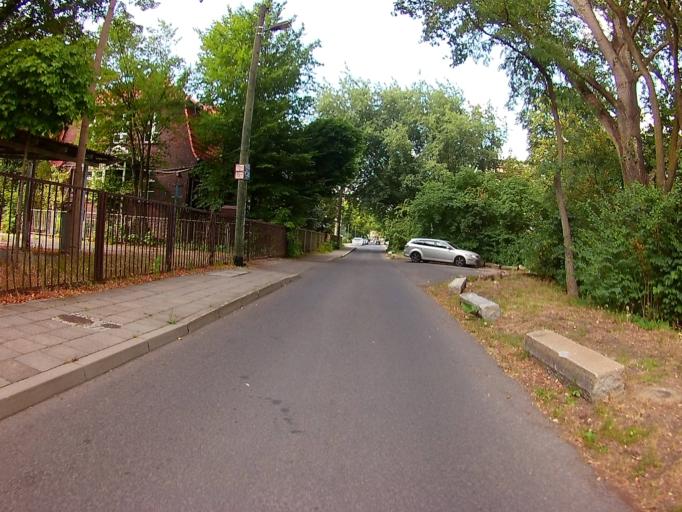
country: DE
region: Berlin
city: Rummelsburg
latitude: 52.4964
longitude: 13.4987
